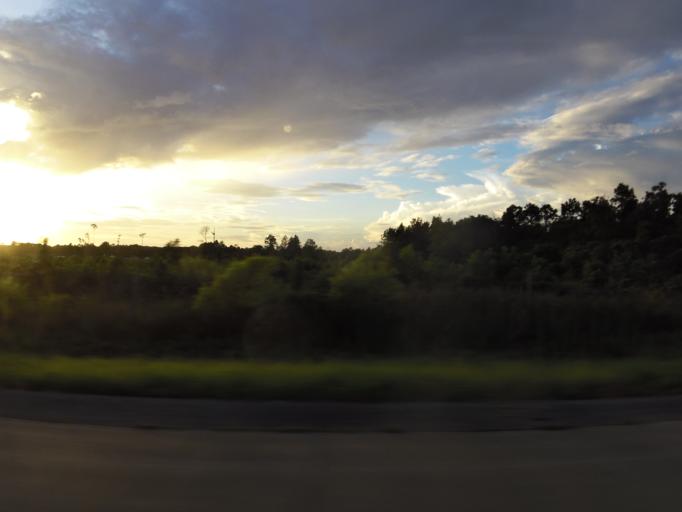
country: US
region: Georgia
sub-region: Glynn County
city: Dock Junction
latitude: 31.2390
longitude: -81.5057
